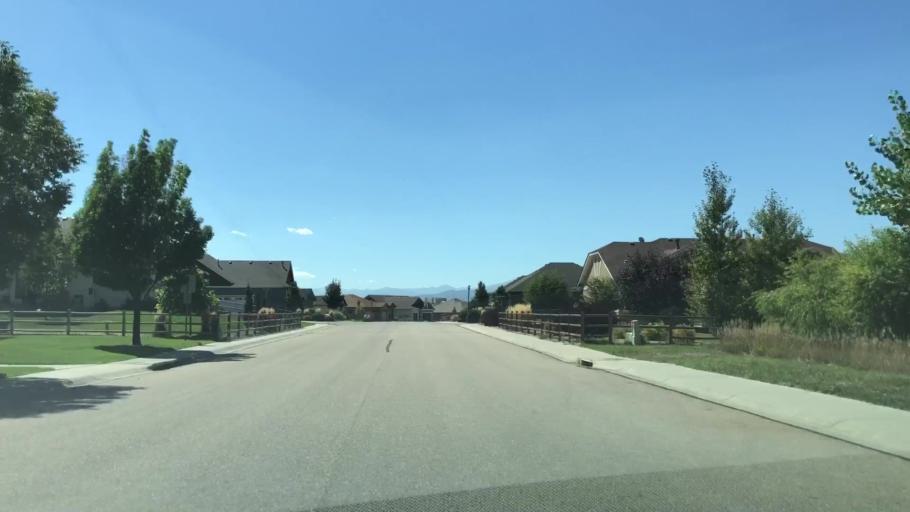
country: US
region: Colorado
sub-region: Weld County
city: Windsor
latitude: 40.4545
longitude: -104.9572
